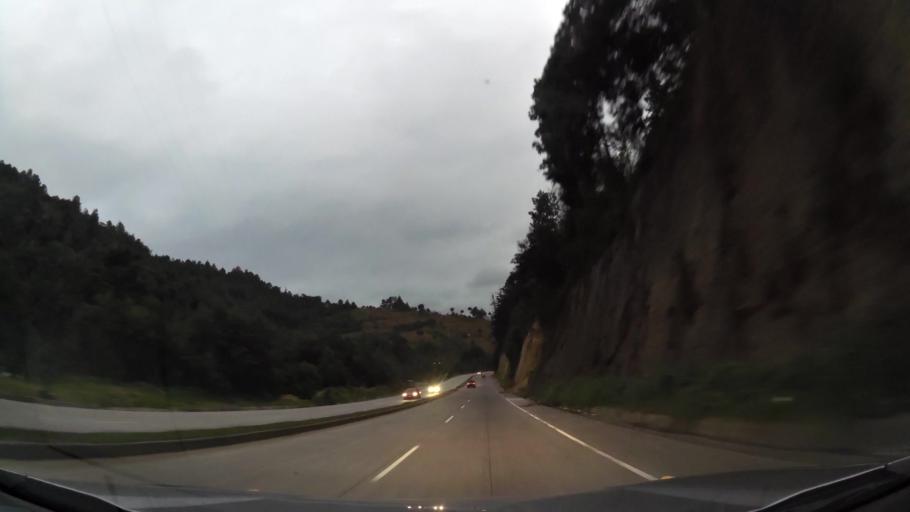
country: GT
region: Chimaltenango
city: Santa Apolonia
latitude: 14.8438
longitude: -91.0427
